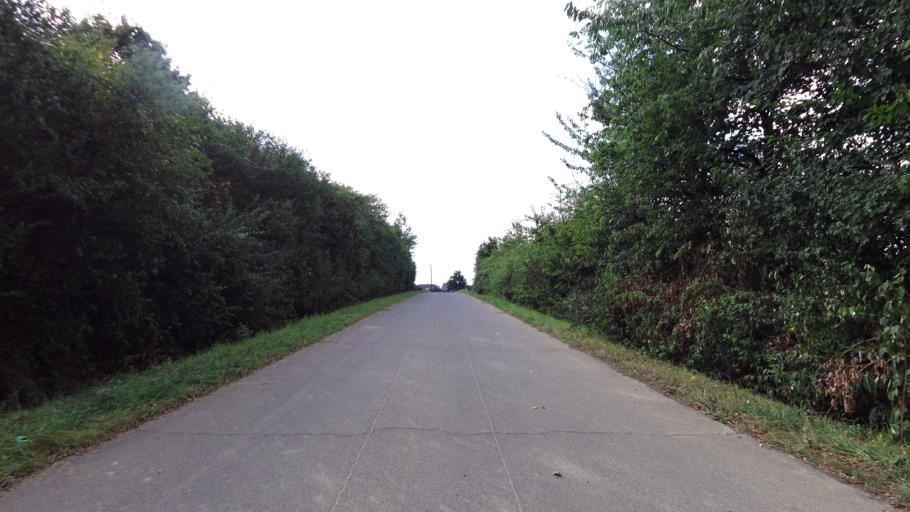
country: DE
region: North Rhine-Westphalia
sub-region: Regierungsbezirk Koln
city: Euskirchen
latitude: 50.6609
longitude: 6.8454
